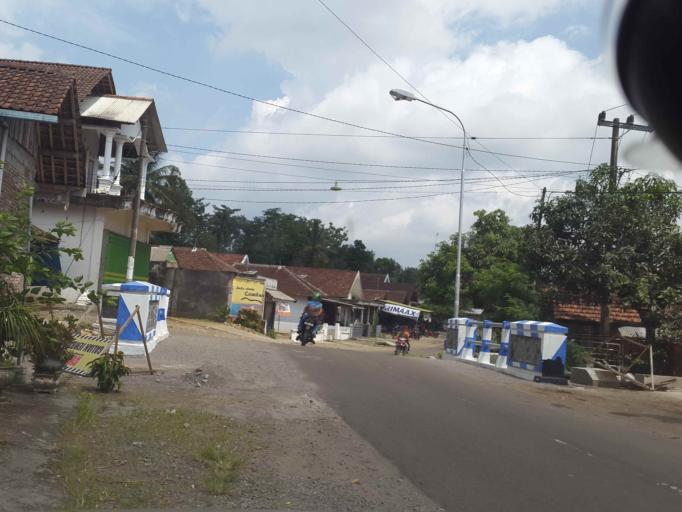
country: ID
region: East Java
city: Resapombo
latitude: -8.0463
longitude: 112.4184
